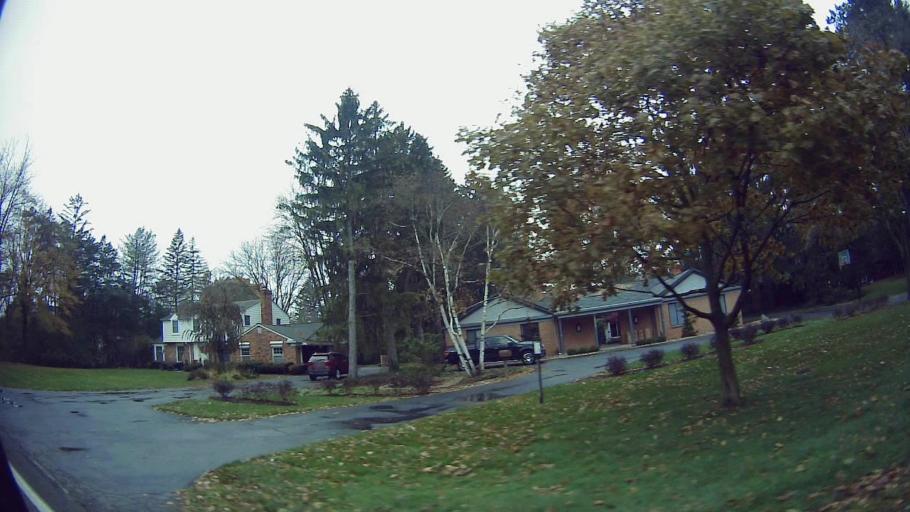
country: US
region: Michigan
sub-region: Oakland County
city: Beverly Hills
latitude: 42.5286
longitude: -83.2446
